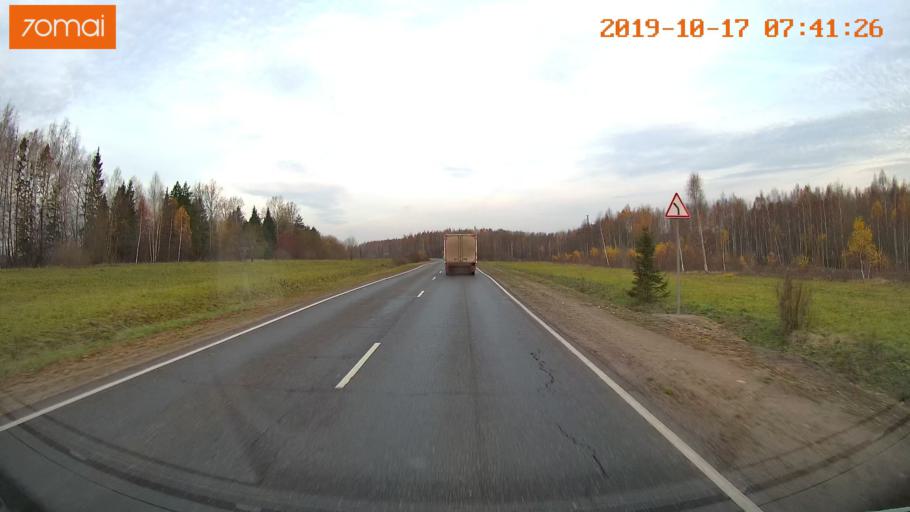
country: RU
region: Vladimir
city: Yur'yev-Pol'skiy
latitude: 56.4819
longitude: 39.8103
